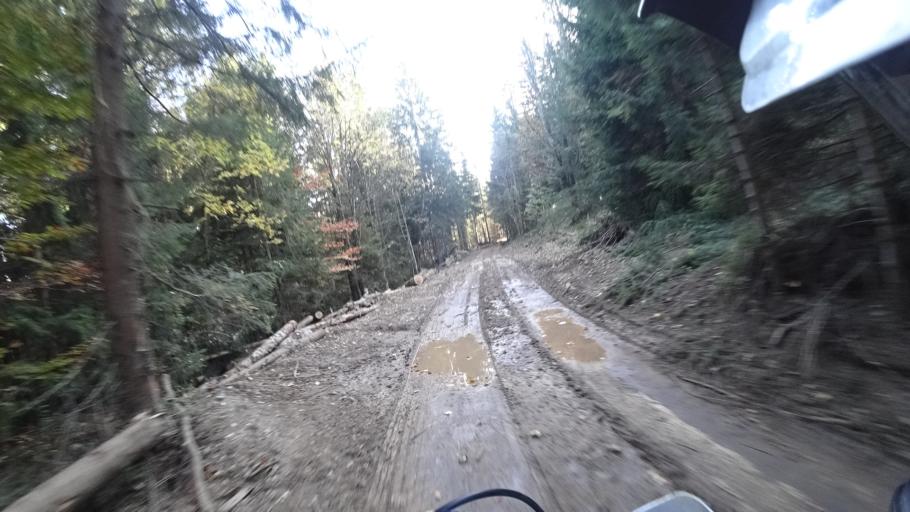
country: HR
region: Karlovacka
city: Plaski
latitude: 44.9518
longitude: 15.4499
